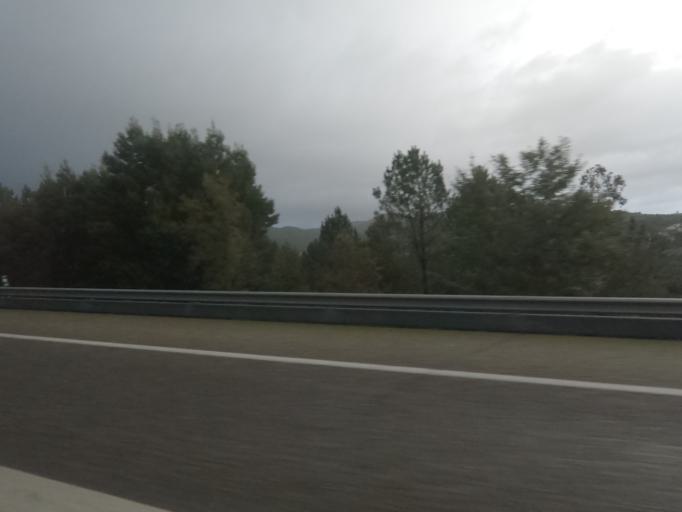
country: PT
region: Viana do Castelo
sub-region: Ponte de Lima
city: Ponte de Lima
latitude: 41.8159
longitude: -8.5995
